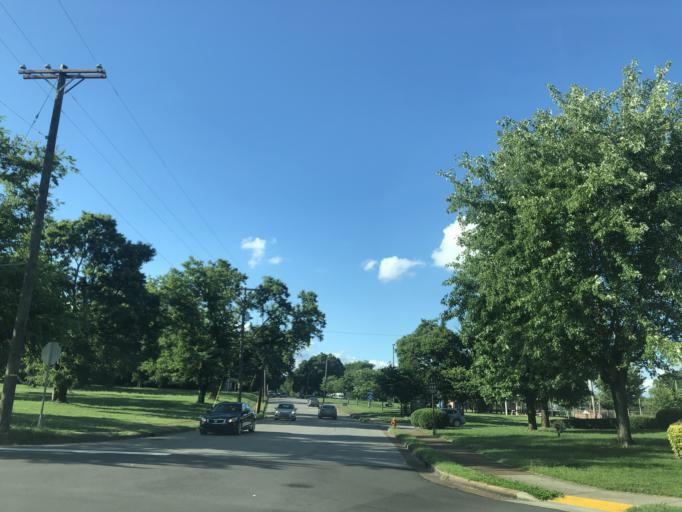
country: US
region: Tennessee
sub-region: Davidson County
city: Nashville
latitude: 36.1858
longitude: -86.7619
